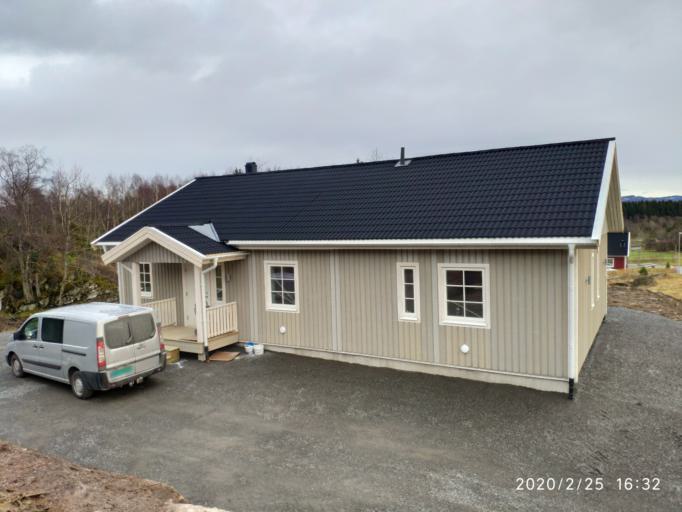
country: NO
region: Rogaland
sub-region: Finnoy
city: Judaberg
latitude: 59.3484
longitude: 5.8688
